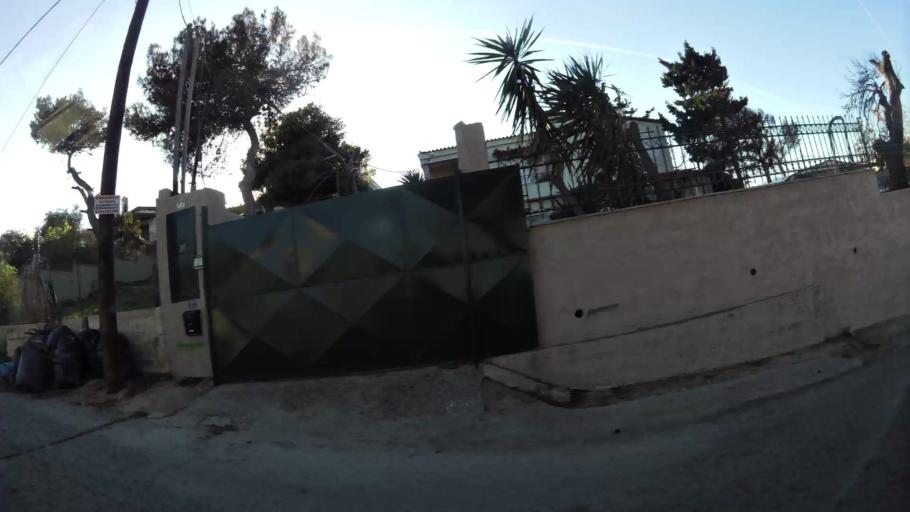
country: GR
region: Attica
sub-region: Nomarchia Anatolikis Attikis
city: Rafina
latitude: 38.0304
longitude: 23.9998
